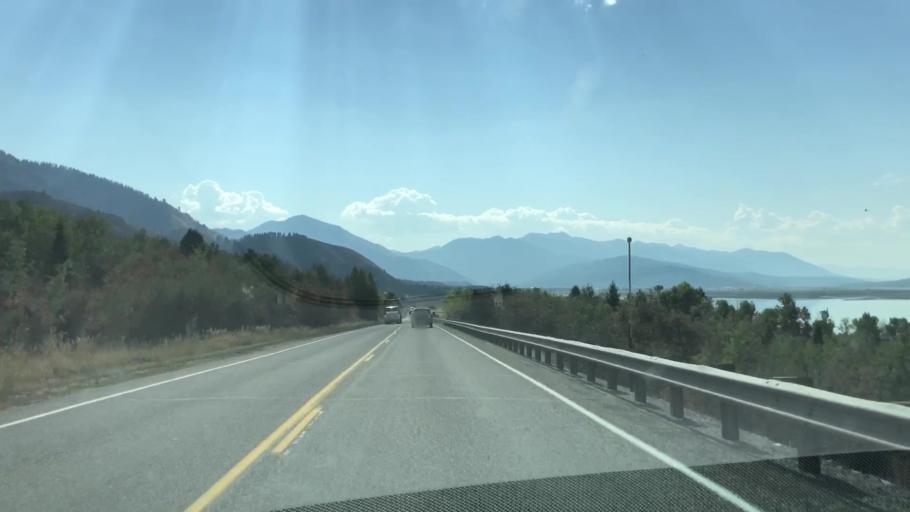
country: US
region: Wyoming
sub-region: Teton County
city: Hoback
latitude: 43.2244
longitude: -111.0780
